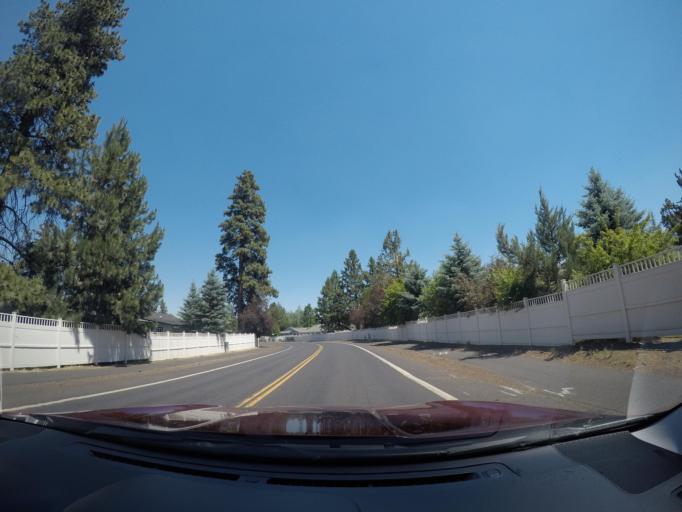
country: US
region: Oregon
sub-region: Deschutes County
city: Sisters
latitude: 44.2944
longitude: -121.5631
